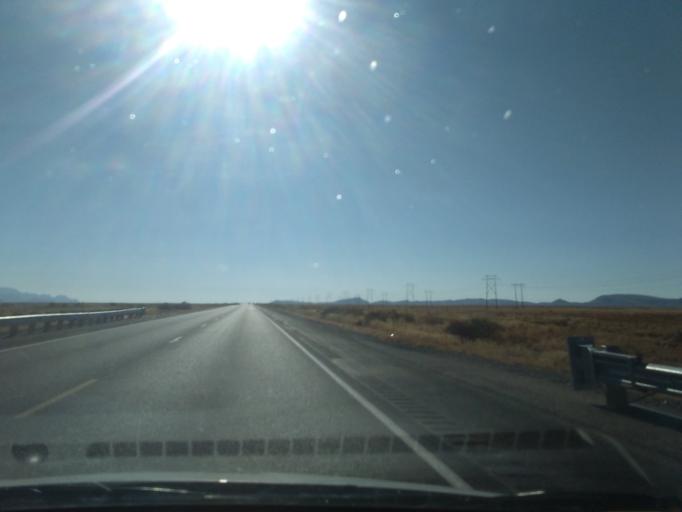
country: US
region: New Mexico
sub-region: Luna County
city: Deming
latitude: 32.4817
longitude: -107.5272
